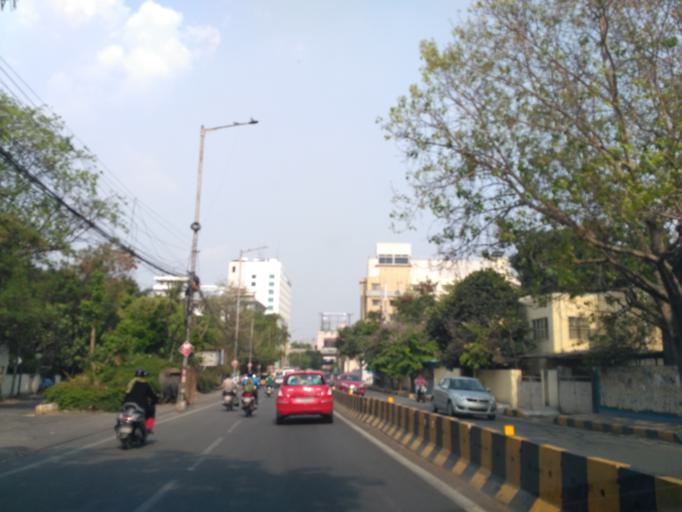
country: IN
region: Telangana
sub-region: Hyderabad
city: Hyderabad
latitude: 17.4173
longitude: 78.4544
